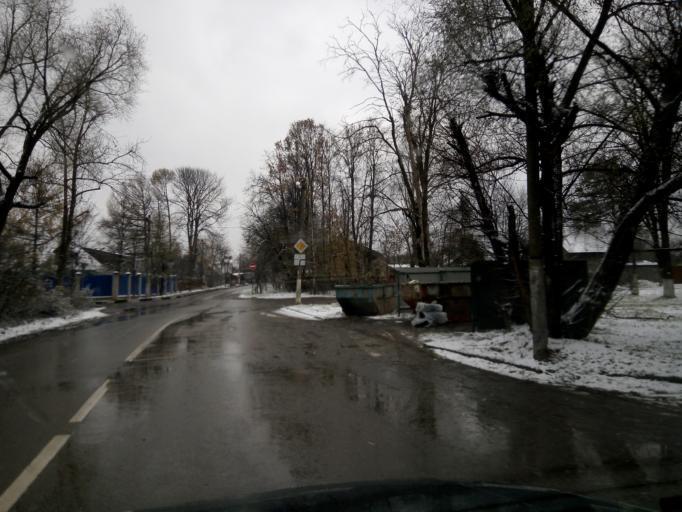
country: RU
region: Moskovskaya
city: Skhodnya
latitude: 55.9462
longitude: 37.2854
